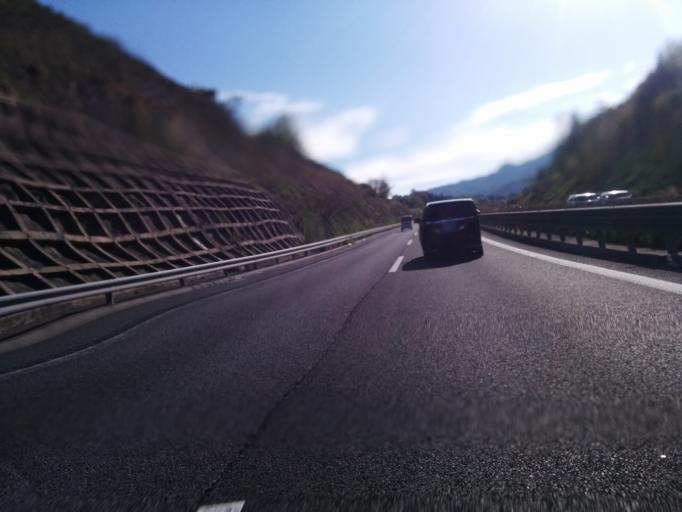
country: JP
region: Shiga Prefecture
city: Kusatsu
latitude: 34.9603
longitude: 135.9823
